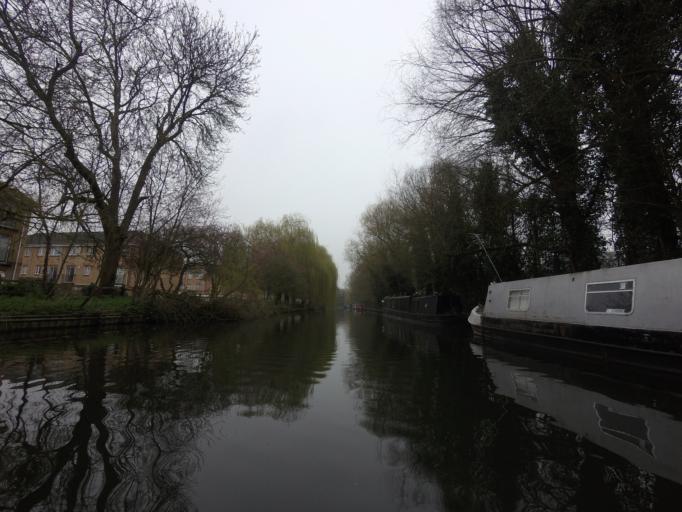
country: GB
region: England
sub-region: Hertfordshire
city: Kings Langley
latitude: 51.7310
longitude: -0.4567
